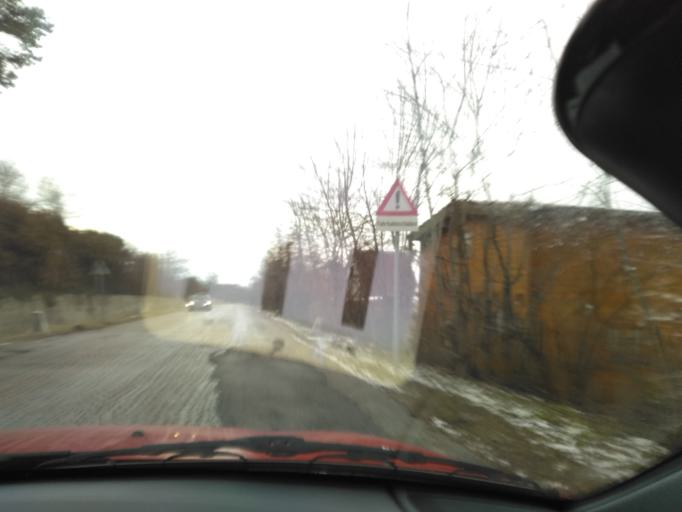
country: AT
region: Lower Austria
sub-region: Politischer Bezirk Wien-Umgebung
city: Klosterneuburg
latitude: 48.2635
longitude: 16.3135
